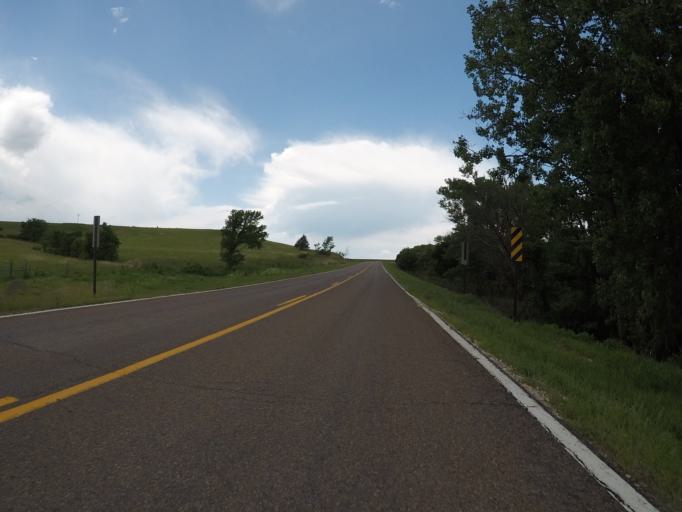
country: US
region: Kansas
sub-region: Wabaunsee County
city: Alma
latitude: 38.8710
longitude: -96.3490
